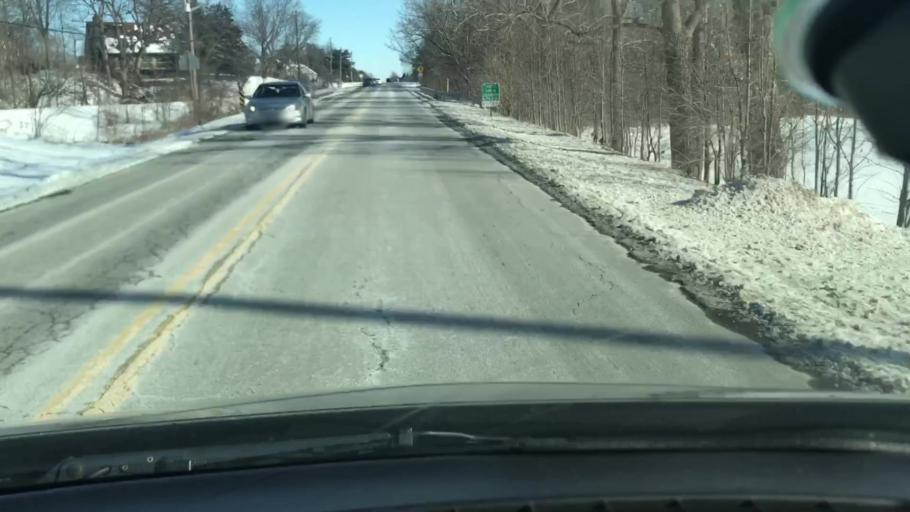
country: US
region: Indiana
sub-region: Hamilton County
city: Carmel
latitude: 39.9712
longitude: -86.0972
